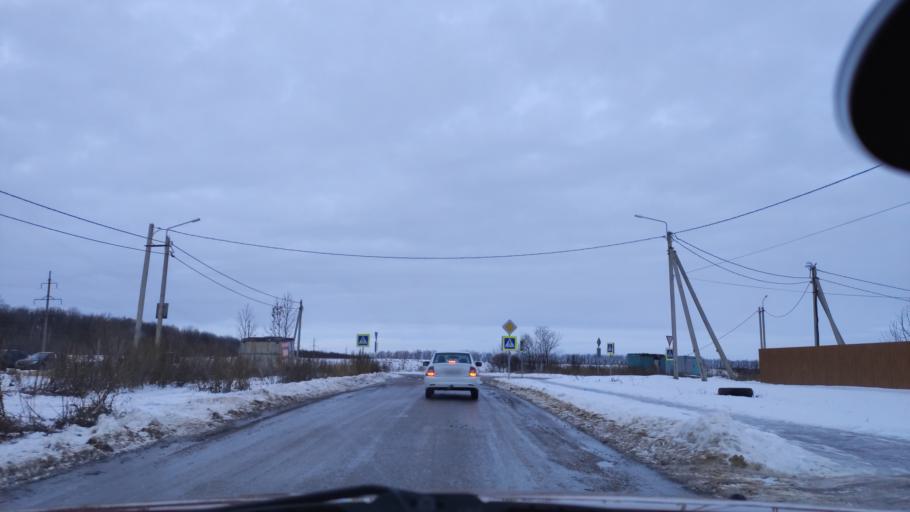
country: RU
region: Tambov
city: Komsomolets
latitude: 52.7603
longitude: 41.3623
